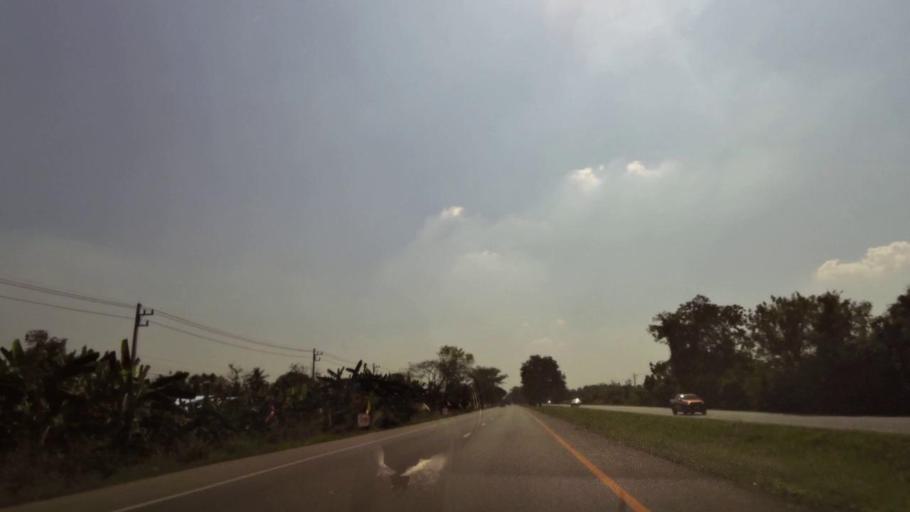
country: TH
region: Phichit
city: Bueng Na Rang
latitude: 16.2384
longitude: 100.1254
